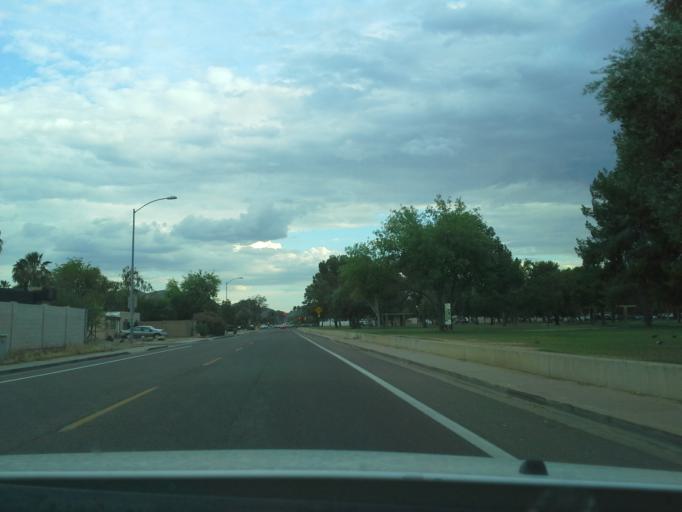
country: US
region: Arizona
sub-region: Maricopa County
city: Paradise Valley
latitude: 33.5996
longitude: -112.0046
